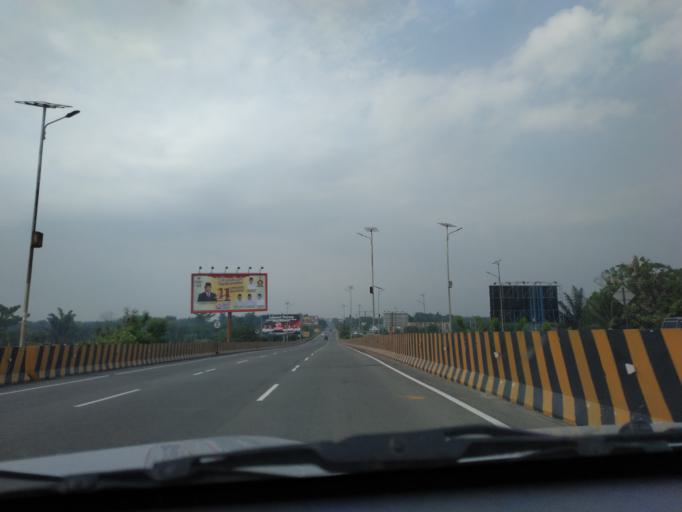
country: ID
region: North Sumatra
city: Percut
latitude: 3.6070
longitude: 98.8509
